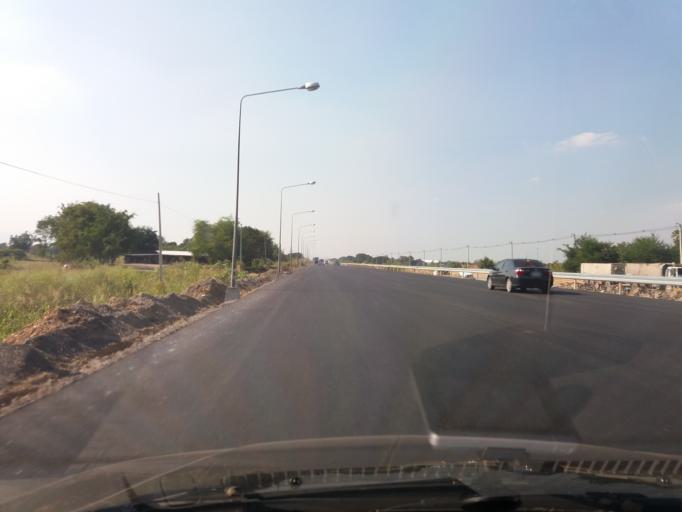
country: TH
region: Nakhon Sawan
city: Krok Phra
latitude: 15.6238
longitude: 100.1120
